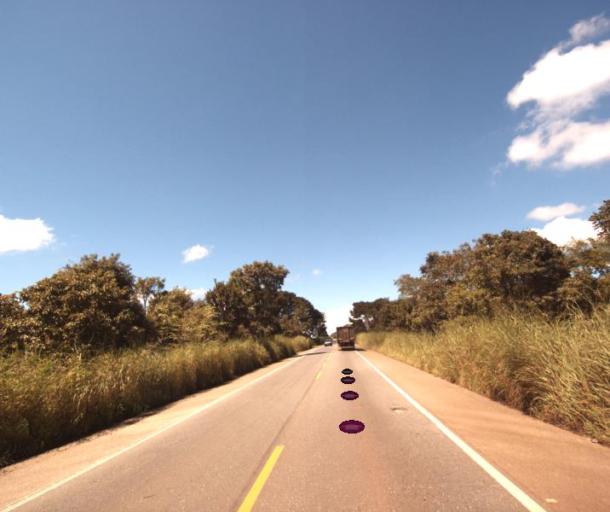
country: BR
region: Goias
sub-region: Jaragua
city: Jaragua
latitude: -15.7192
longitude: -49.3290
